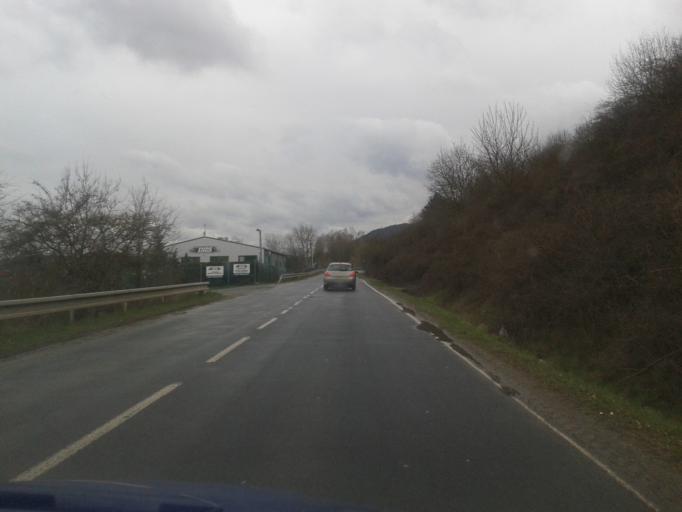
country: CZ
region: Central Bohemia
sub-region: Okres Beroun
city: Lodenice
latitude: 50.0048
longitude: 14.1789
